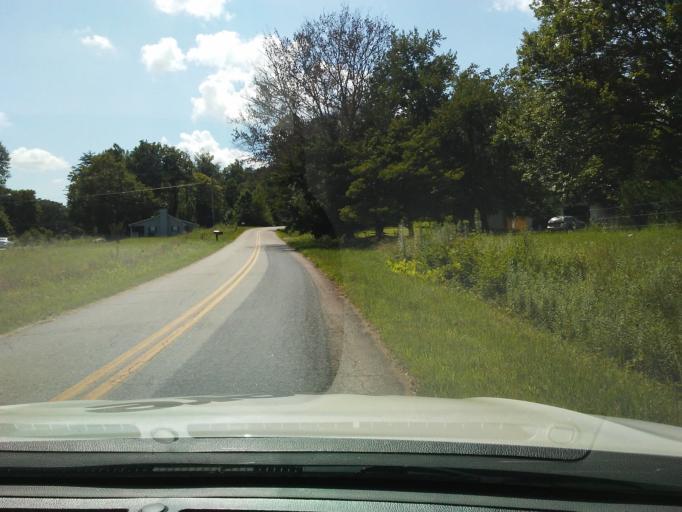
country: US
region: Georgia
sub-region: Union County
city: Blairsville
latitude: 34.9362
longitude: -83.8792
